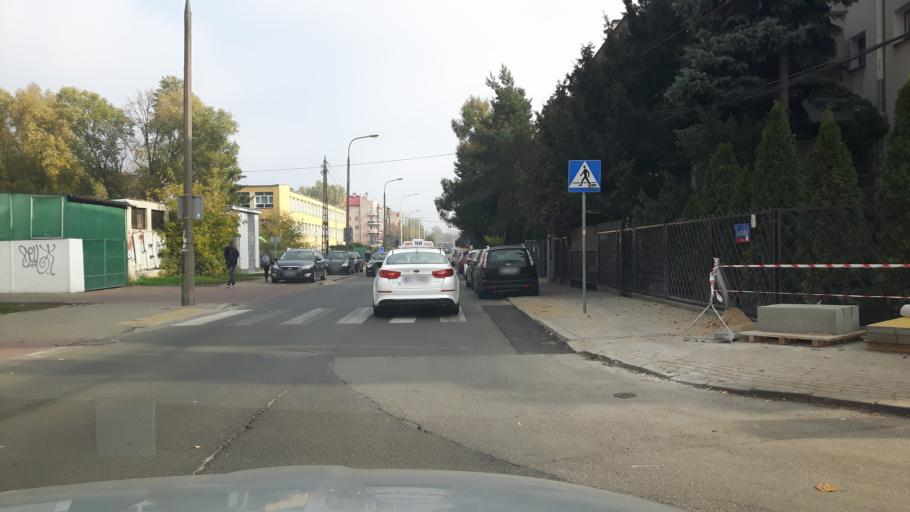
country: PL
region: Masovian Voivodeship
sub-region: Warszawa
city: Wlochy
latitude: 52.1923
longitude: 20.9638
